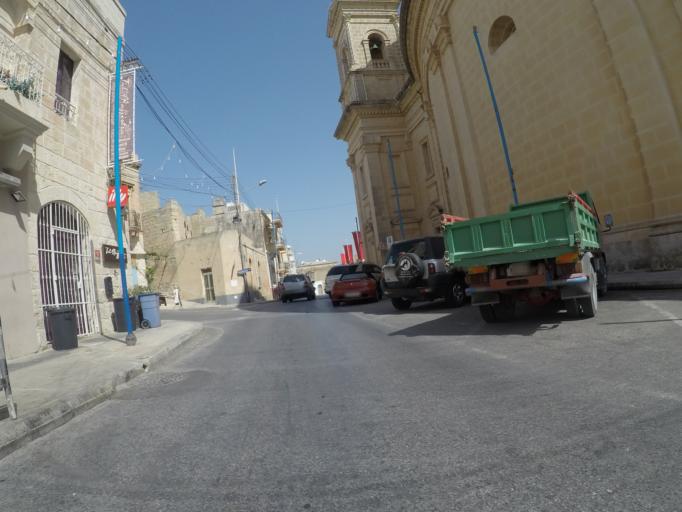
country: MT
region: L-Imgarr
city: Imgarr
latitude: 35.9197
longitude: 14.3660
